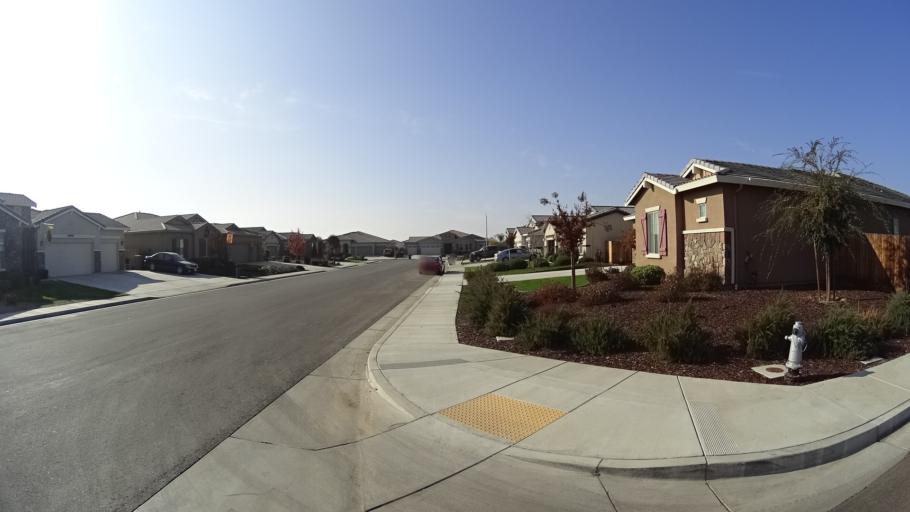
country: US
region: California
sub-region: Kern County
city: Rosedale
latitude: 35.3485
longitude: -119.1715
